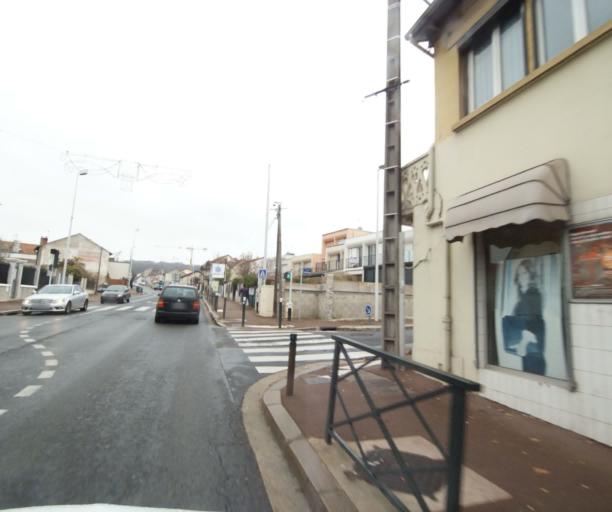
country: FR
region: Ile-de-France
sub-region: Departement des Hauts-de-Seine
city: Nanterre
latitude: 48.8826
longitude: 2.2043
